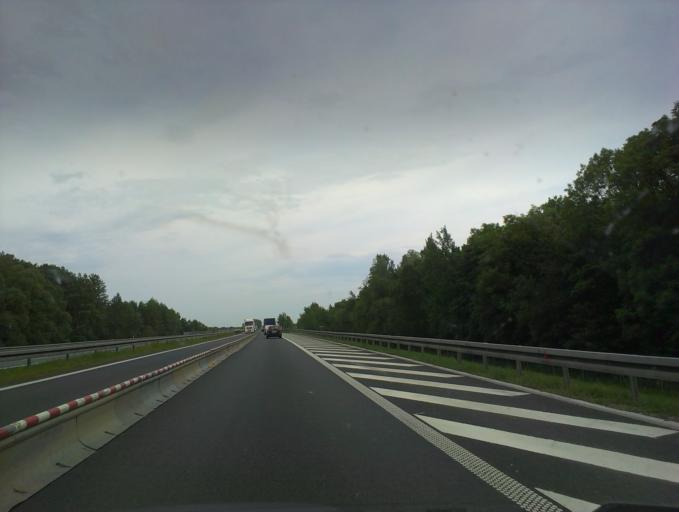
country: PL
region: Opole Voivodeship
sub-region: Powiat brzeski
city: Olszanka
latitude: 50.7282
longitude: 17.5115
